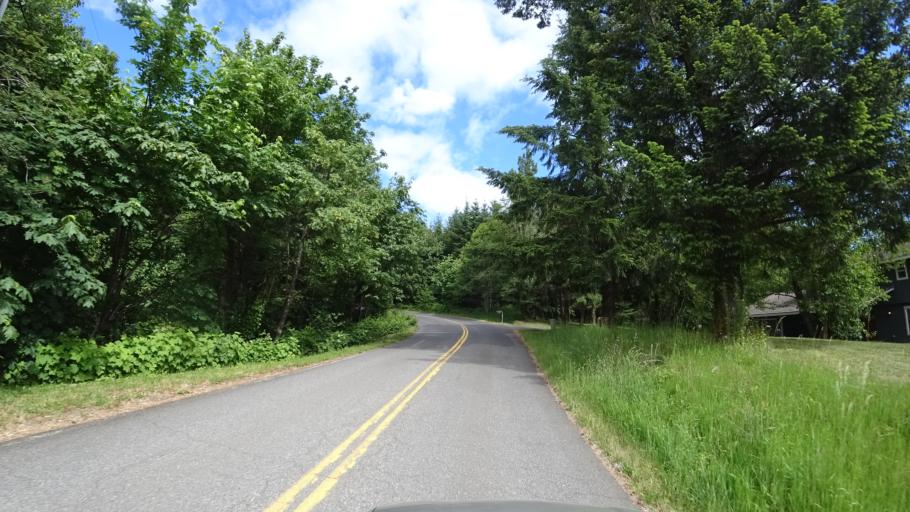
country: US
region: Oregon
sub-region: Washington County
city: Bethany
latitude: 45.6089
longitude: -122.8353
